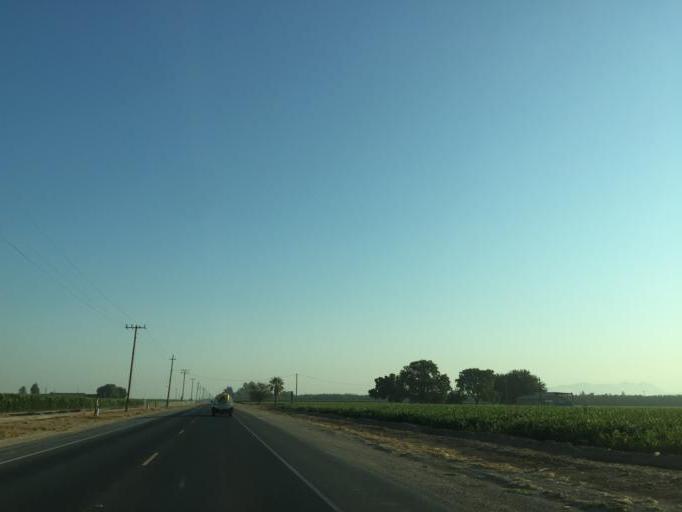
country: US
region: California
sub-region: Tulare County
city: Ivanhoe
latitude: 36.4141
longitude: -119.2961
